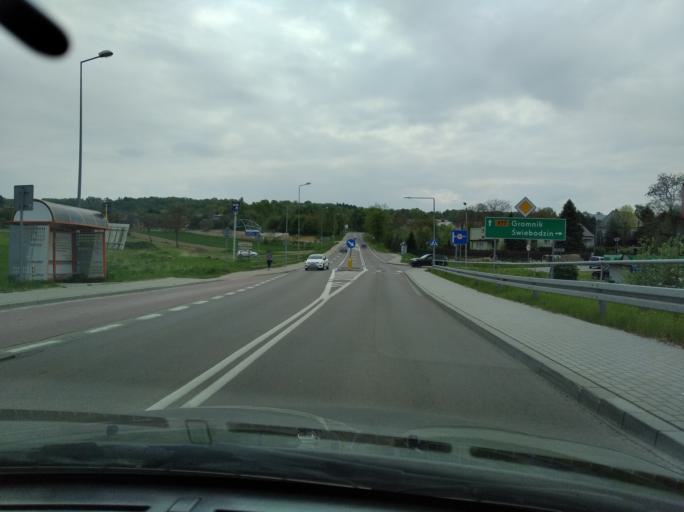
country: PL
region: Lesser Poland Voivodeship
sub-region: Powiat tarnowski
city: Tarnowiec
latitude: 49.9717
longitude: 20.9912
